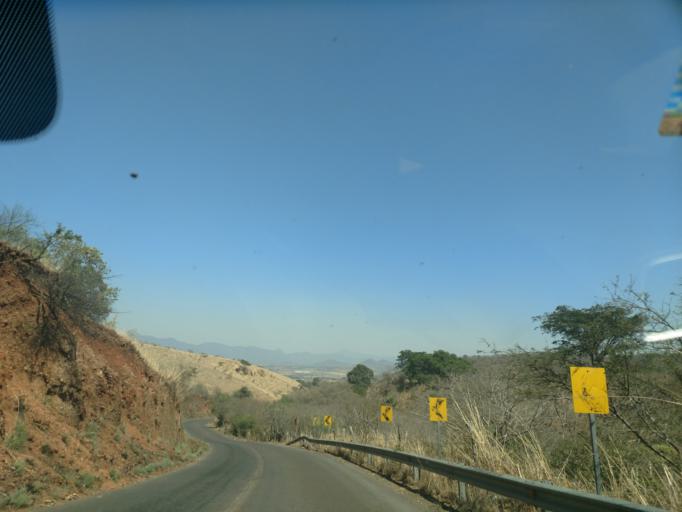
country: MX
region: Nayarit
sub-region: Tepic
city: La Corregidora
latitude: 21.4827
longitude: -104.6774
